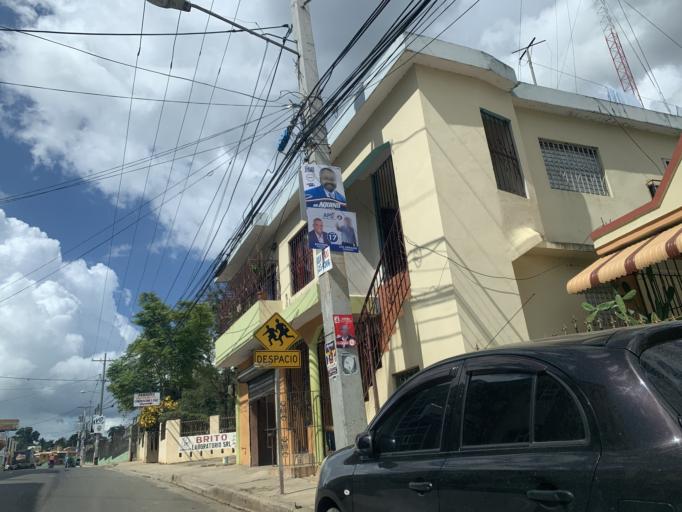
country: DO
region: Monte Plata
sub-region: Yamasa
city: Yamasa
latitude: 18.7668
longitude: -70.0228
